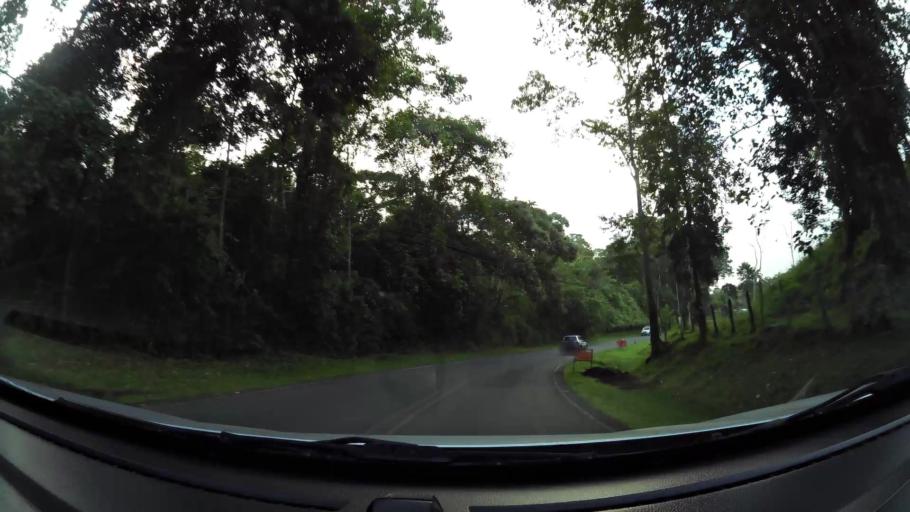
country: CR
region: Cartago
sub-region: Canton de Turrialba
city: La Suiza
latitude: 9.9649
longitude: -83.5697
